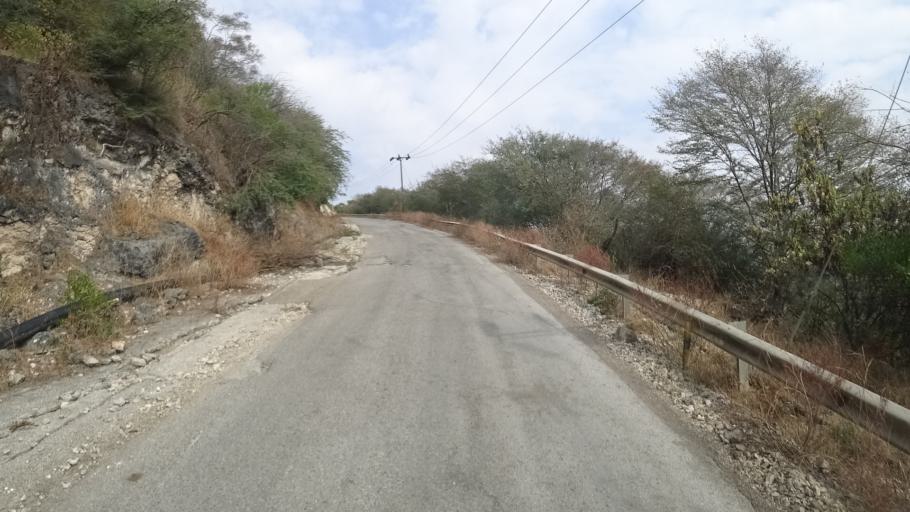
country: YE
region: Al Mahrah
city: Hawf
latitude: 16.7248
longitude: 53.2730
